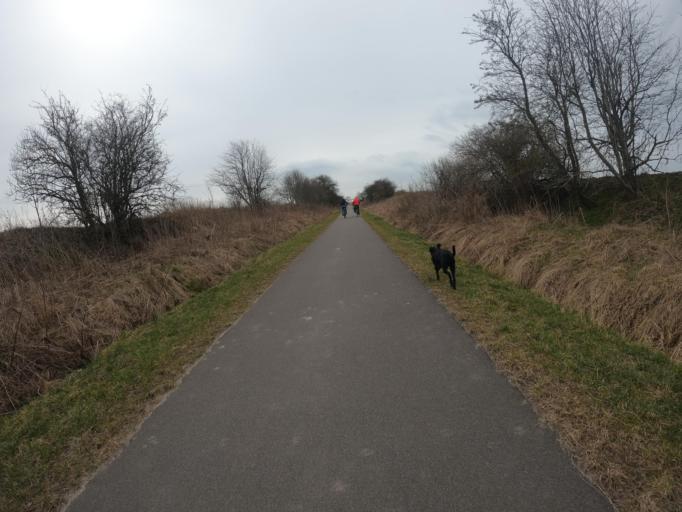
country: PL
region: West Pomeranian Voivodeship
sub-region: Powiat gryficki
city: Mrzezyno
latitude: 54.1149
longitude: 15.3014
